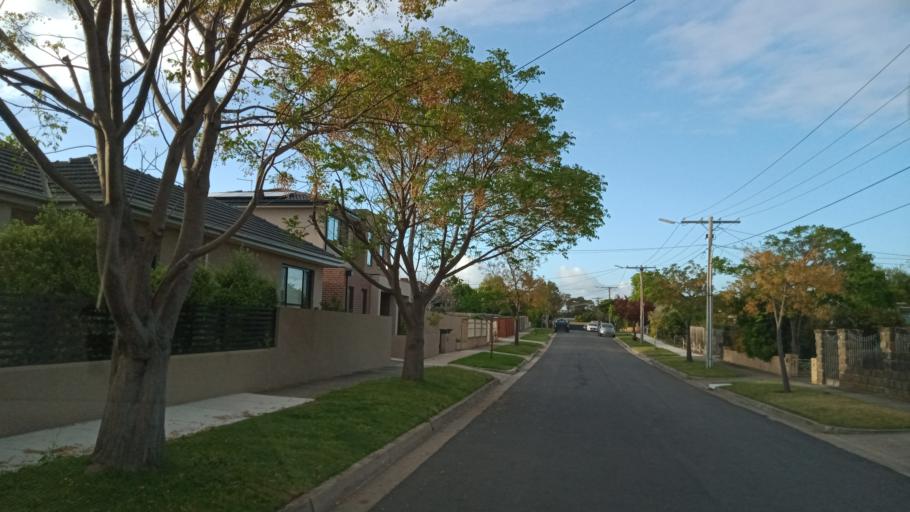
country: AU
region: Victoria
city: McKinnon
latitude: -37.9303
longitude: 145.0534
